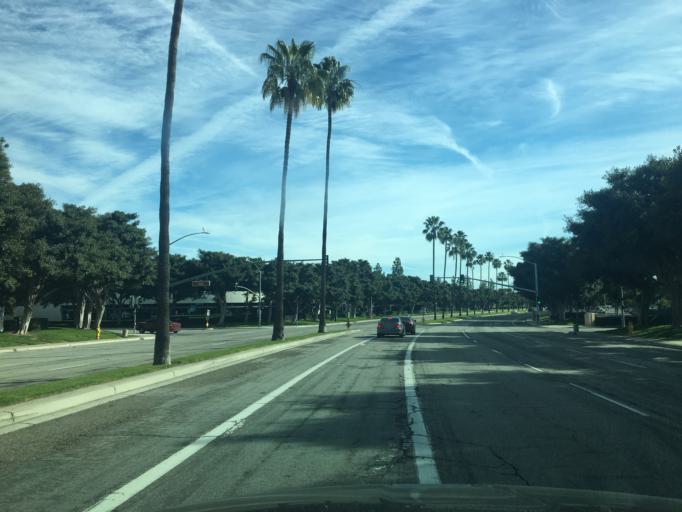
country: US
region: California
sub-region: Orange County
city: Laguna Woods
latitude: 33.6545
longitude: -117.7381
